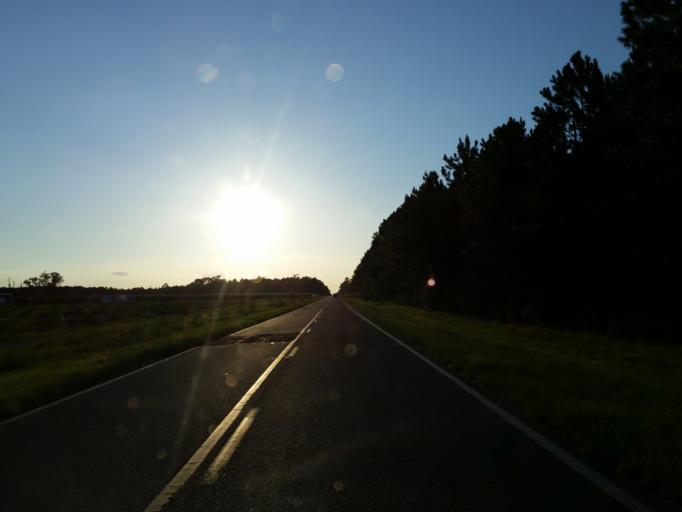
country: US
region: Georgia
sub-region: Lanier County
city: Lakeland
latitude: 31.1642
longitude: -83.0897
